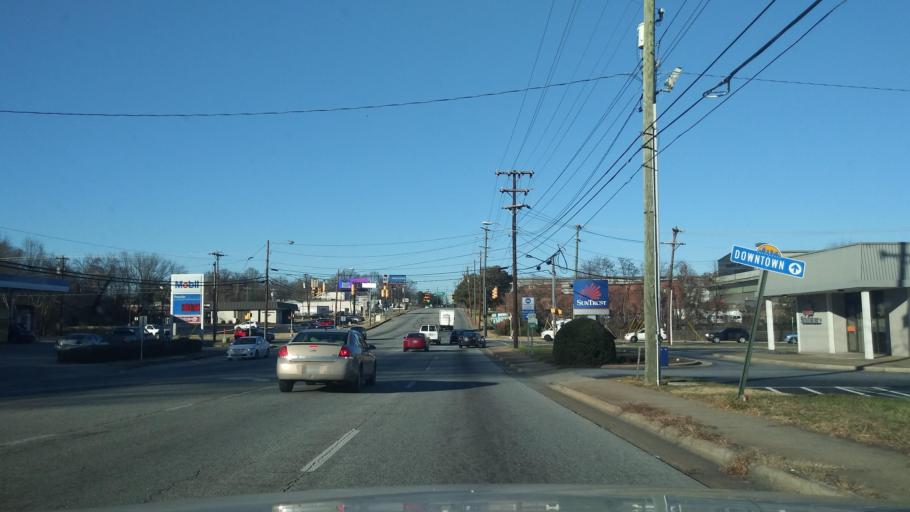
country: US
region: North Carolina
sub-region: Guilford County
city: Greensboro
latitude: 36.0481
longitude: -79.7914
